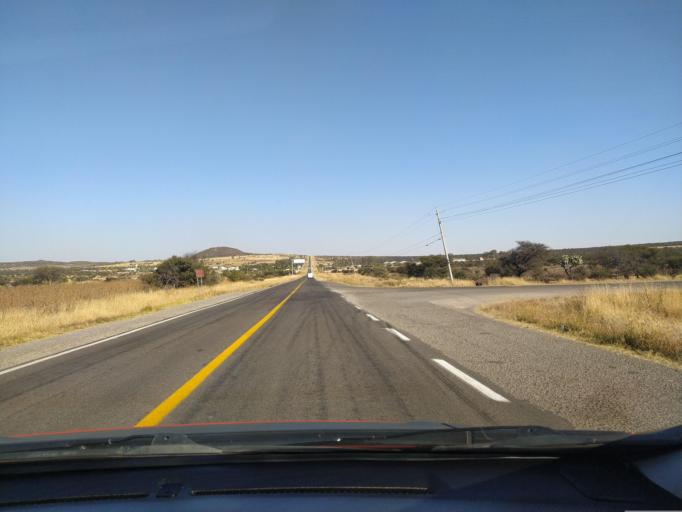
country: MX
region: Jalisco
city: San Miguel el Alto
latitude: 21.0194
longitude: -102.4578
